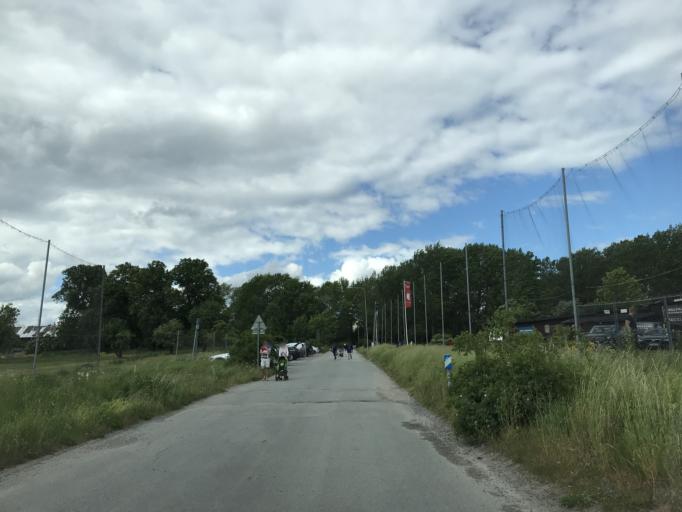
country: SE
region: Stockholm
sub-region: Solna Kommun
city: Rasunda
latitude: 59.3860
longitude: 17.9979
